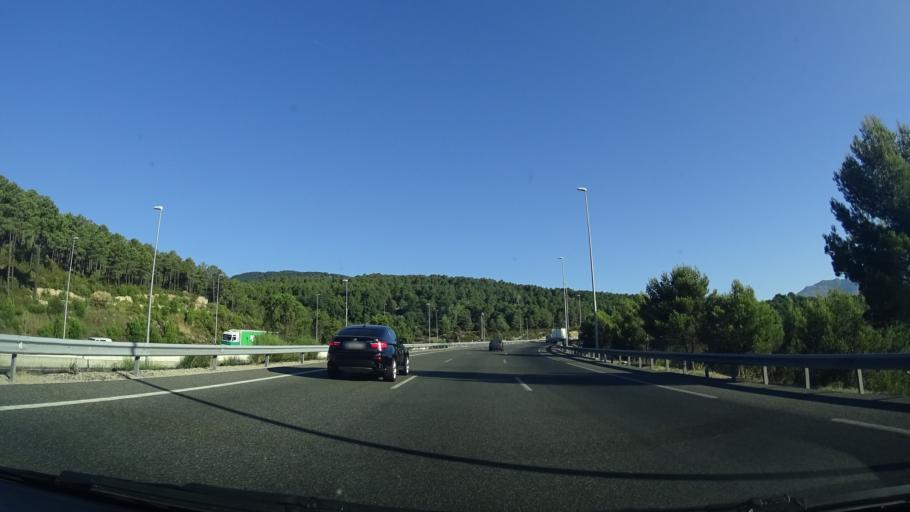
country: ES
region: Madrid
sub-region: Provincia de Madrid
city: Guadarrama
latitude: 40.6783
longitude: -4.1169
